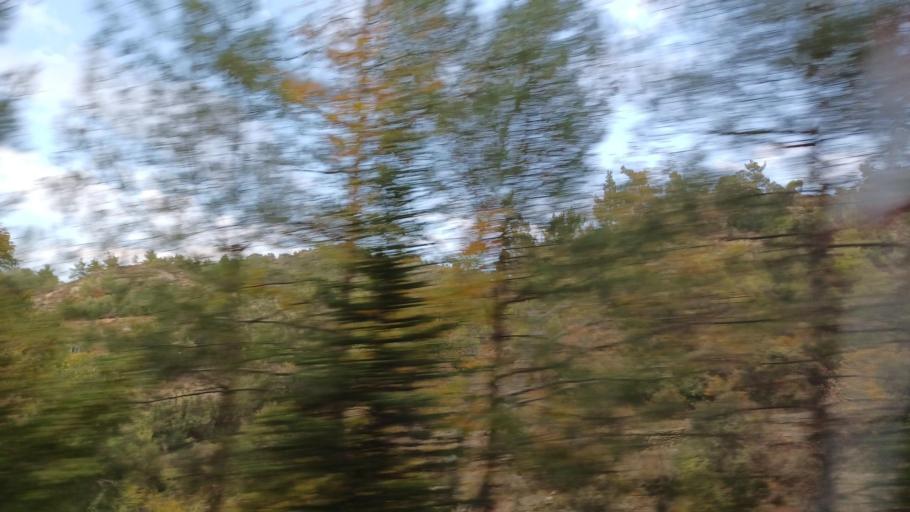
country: CY
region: Lefkosia
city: Kakopetria
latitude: 34.9741
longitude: 32.9132
